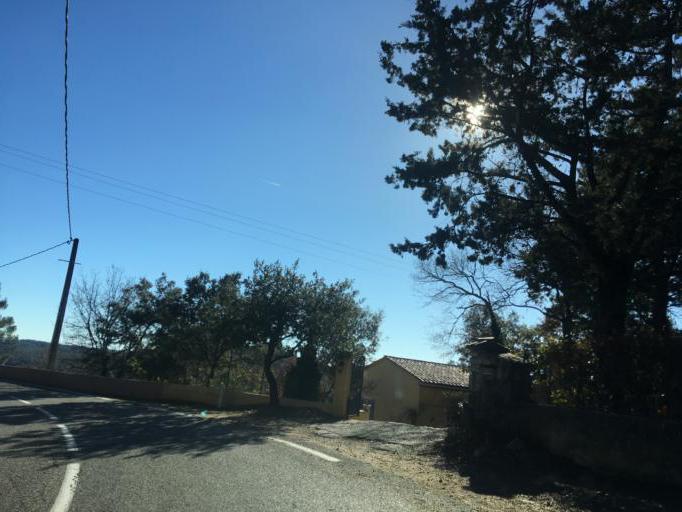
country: FR
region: Provence-Alpes-Cote d'Azur
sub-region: Departement du Var
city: Barjols
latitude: 43.6006
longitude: 5.9531
